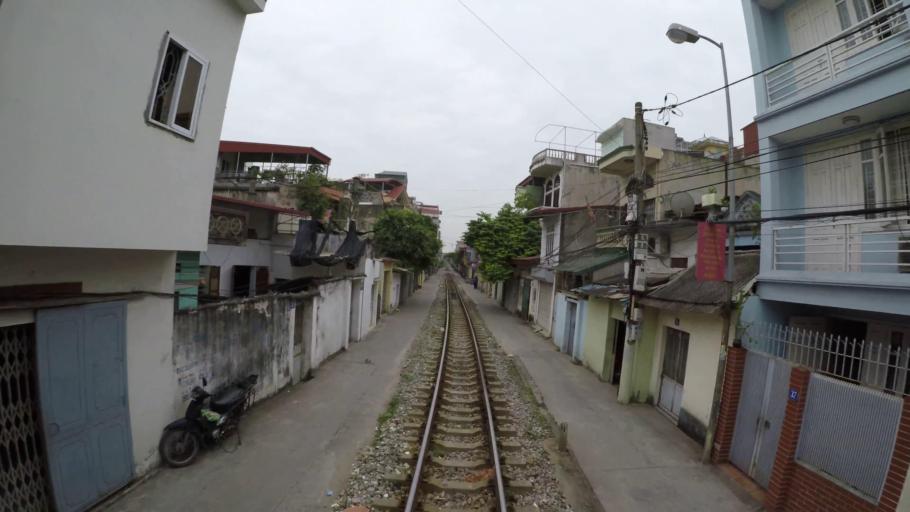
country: VN
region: Hai Phong
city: Haiphong
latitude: 20.8672
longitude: 106.6565
